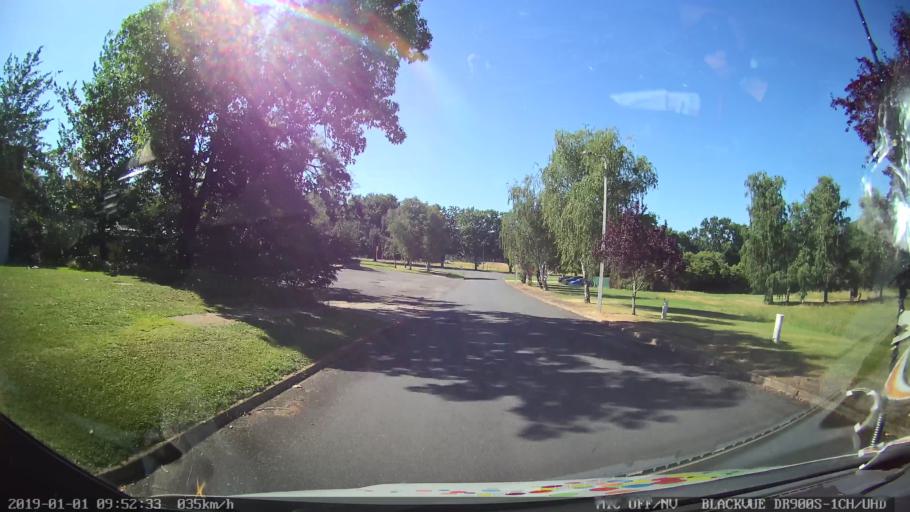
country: AU
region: New South Wales
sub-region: Snowy River
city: Jindabyne
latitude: -36.2186
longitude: 148.1245
